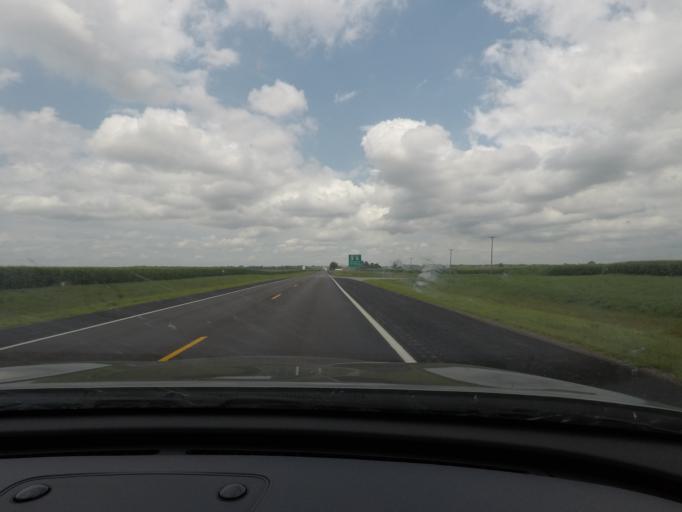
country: US
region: Missouri
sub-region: Carroll County
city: Carrollton
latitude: 39.3261
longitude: -93.4958
